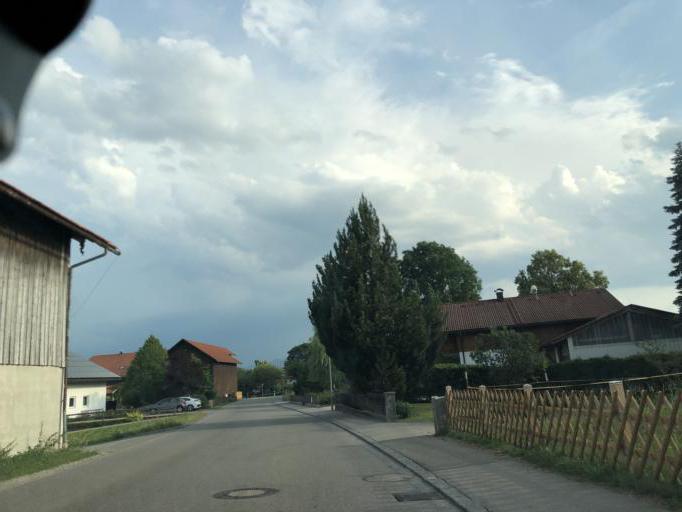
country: DE
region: Bavaria
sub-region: Swabia
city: Gorisried
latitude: 47.7096
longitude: 10.5089
